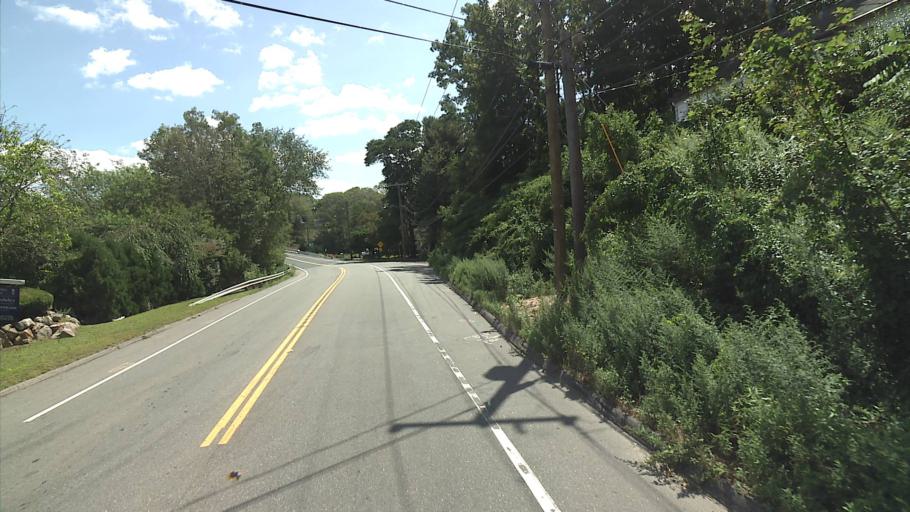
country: US
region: Connecticut
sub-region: New London County
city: Niantic
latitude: 41.3694
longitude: -72.1947
